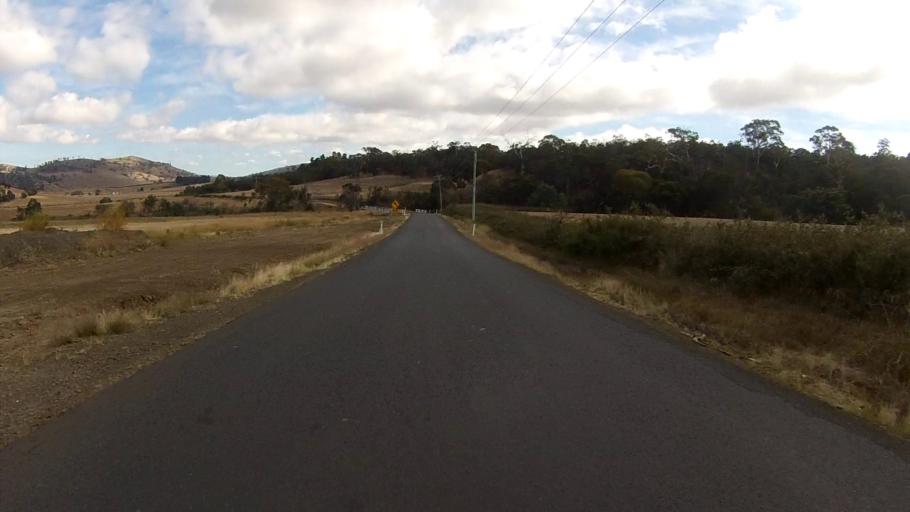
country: AU
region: Tasmania
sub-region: Brighton
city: Old Beach
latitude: -42.7548
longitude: 147.3050
